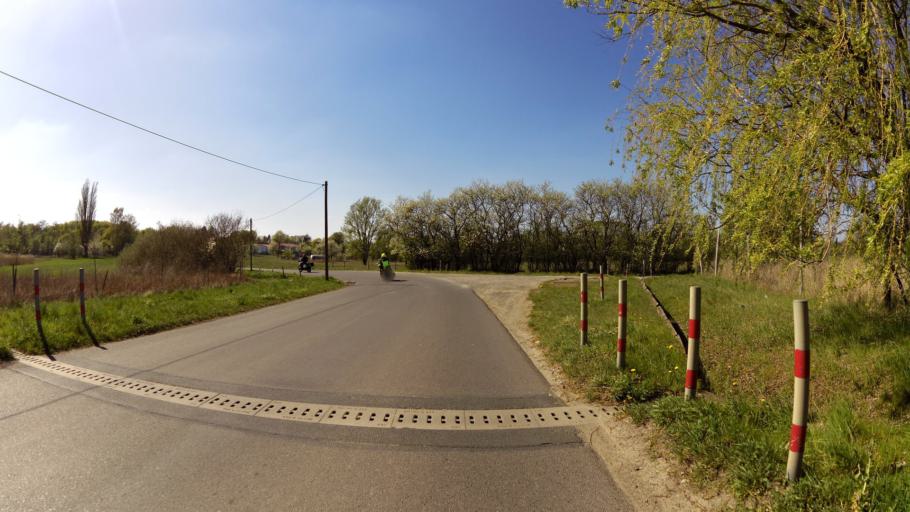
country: DE
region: Brandenburg
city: Muncheberg
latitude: 52.5102
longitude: 14.1428
